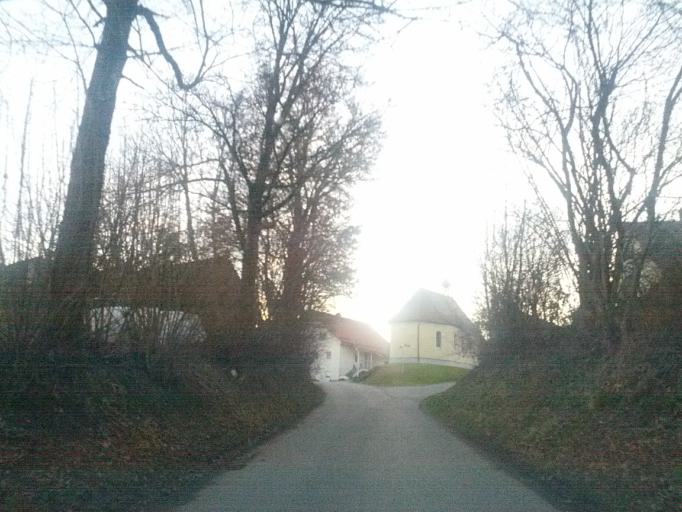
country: DE
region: Baden-Wuerttemberg
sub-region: Tuebingen Region
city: Steinhausen an der Rottum
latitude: 47.9867
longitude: 9.9859
